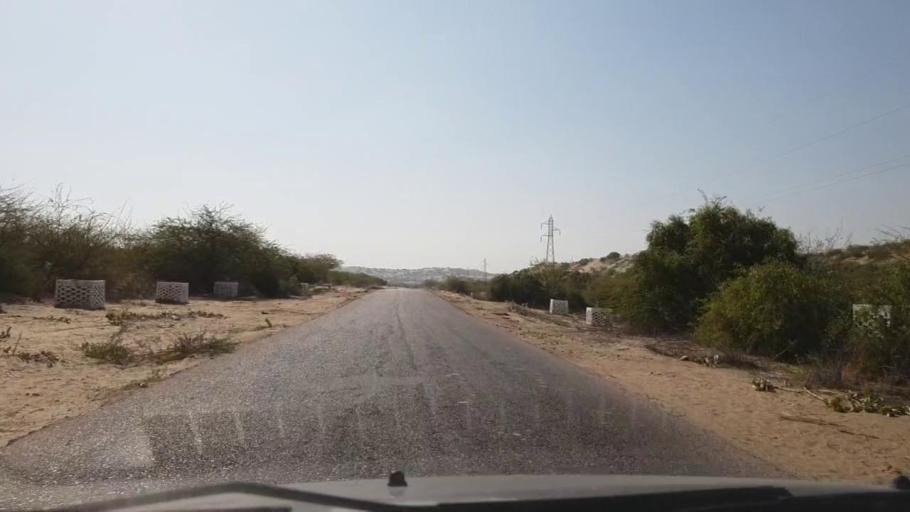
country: PK
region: Sindh
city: Diplo
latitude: 24.4866
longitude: 69.5875
